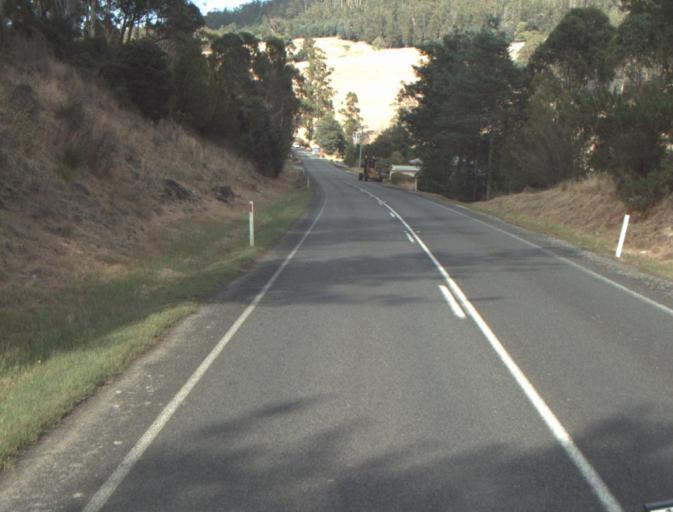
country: AU
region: Tasmania
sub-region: Launceston
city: Mayfield
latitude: -41.2644
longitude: 147.2161
